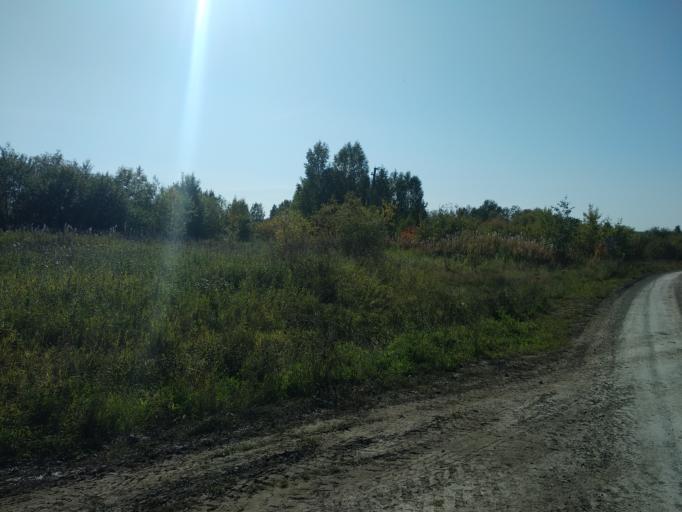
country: RU
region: Sverdlovsk
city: Serov
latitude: 59.7358
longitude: 60.5814
